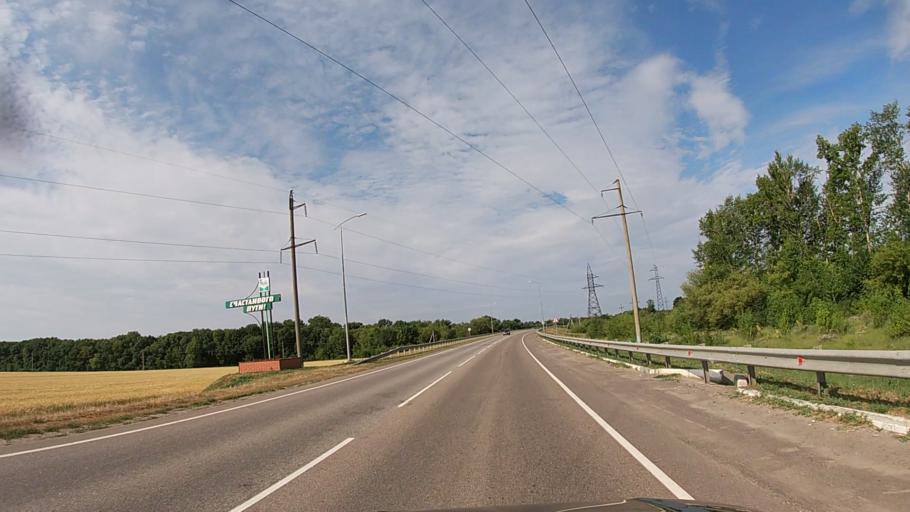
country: RU
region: Belgorod
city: Proletarskiy
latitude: 50.8050
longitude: 35.7409
